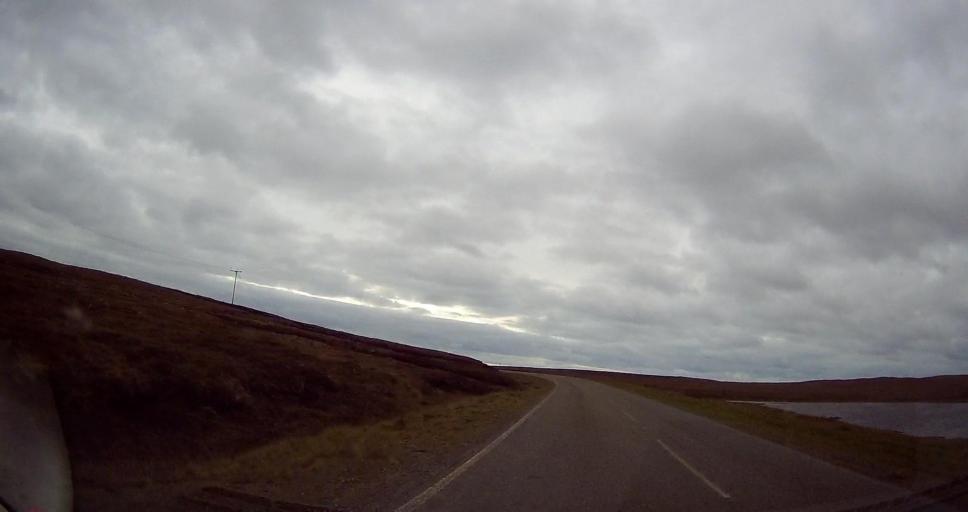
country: GB
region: Scotland
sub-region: Shetland Islands
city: Shetland
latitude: 60.6654
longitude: -1.0290
